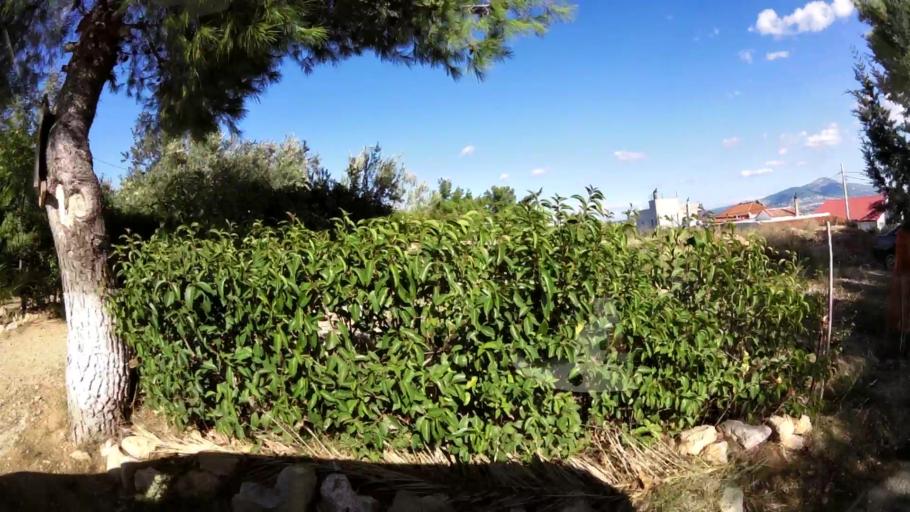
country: GR
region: Attica
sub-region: Nomarchia Anatolikis Attikis
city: Acharnes
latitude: 38.1063
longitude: 23.7200
